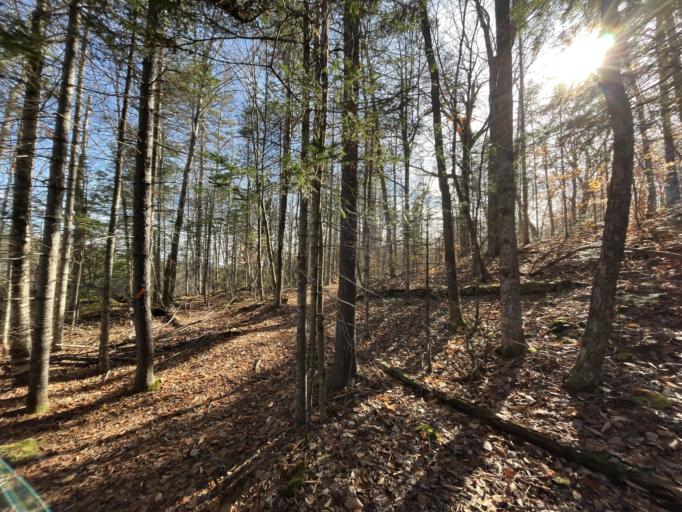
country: US
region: New Hampshire
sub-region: Merrimack County
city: New London
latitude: 43.3980
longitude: -71.9931
